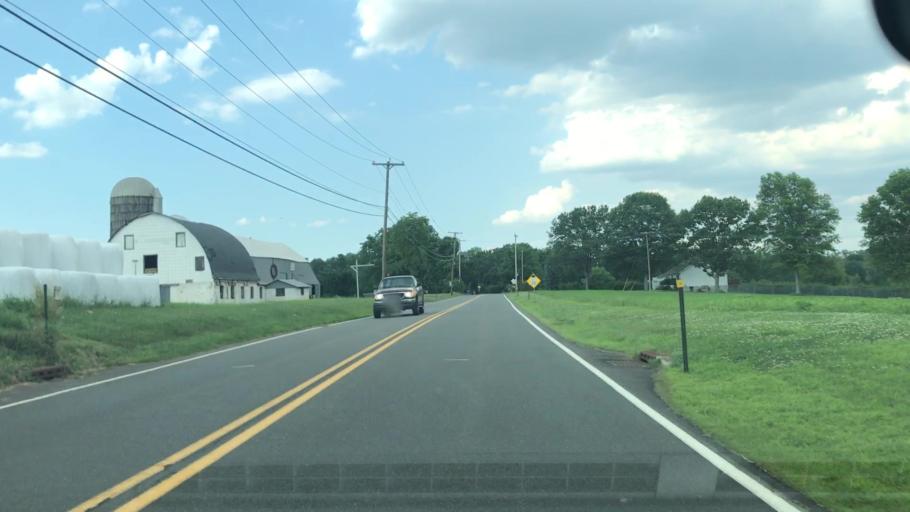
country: US
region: New Jersey
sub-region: Hunterdon County
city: Flemington
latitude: 40.4746
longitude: -74.8211
